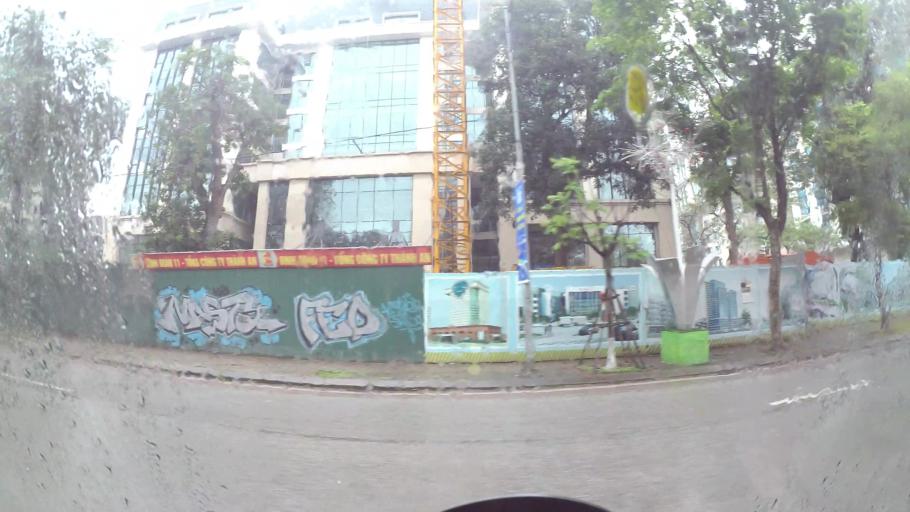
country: VN
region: Ha Noi
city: Hoan Kiem
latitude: 21.0226
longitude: 105.8544
